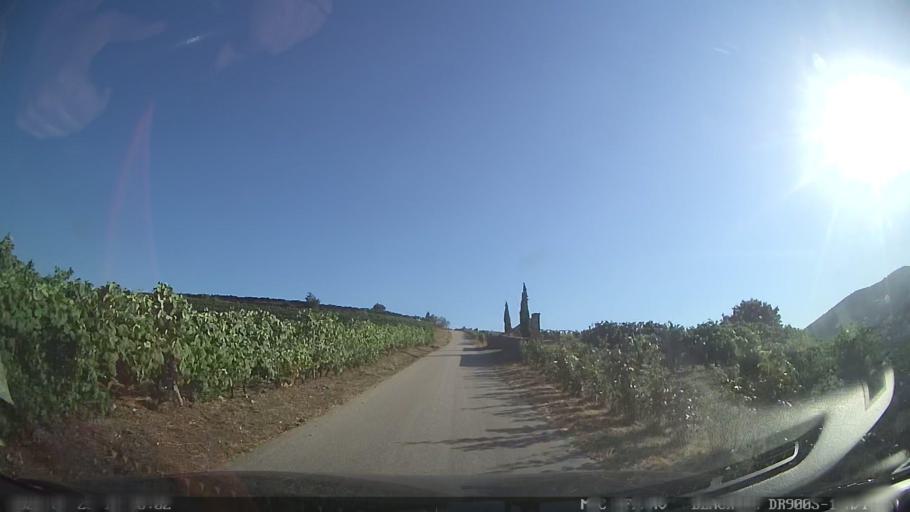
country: PT
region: Viseu
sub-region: Sao Joao da Pesqueira
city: Sao Joao da Pesqueira
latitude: 41.1818
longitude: -7.4028
